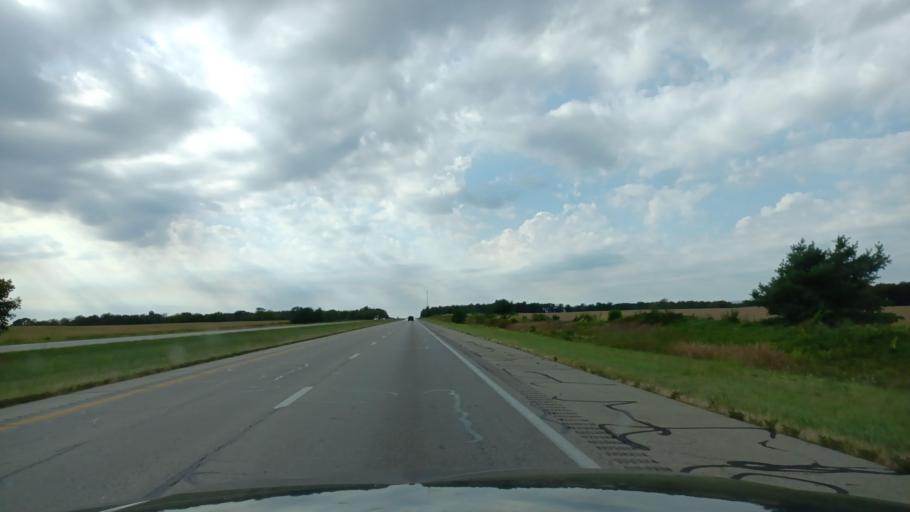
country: US
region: Ohio
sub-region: Ross County
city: Frankfort
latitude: 39.4643
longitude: -83.2490
